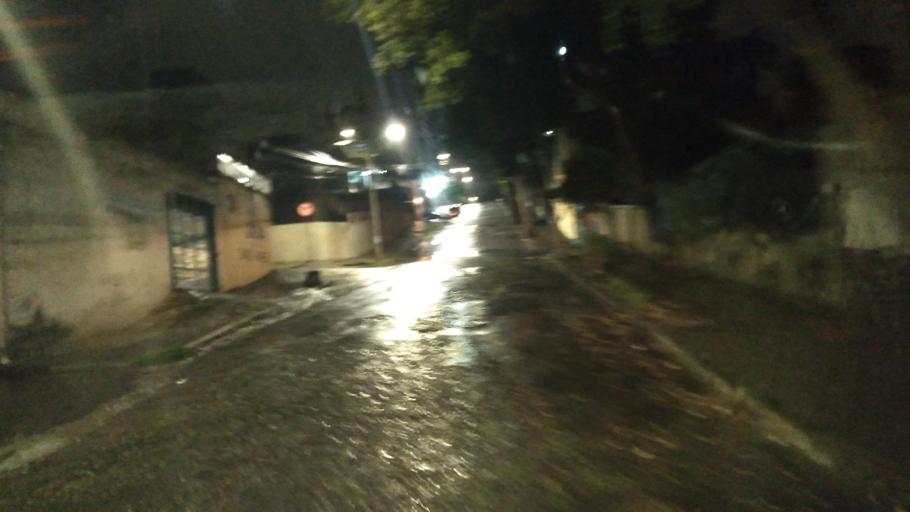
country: BR
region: Minas Gerais
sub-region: Belo Horizonte
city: Belo Horizonte
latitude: -19.9118
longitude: -43.9764
